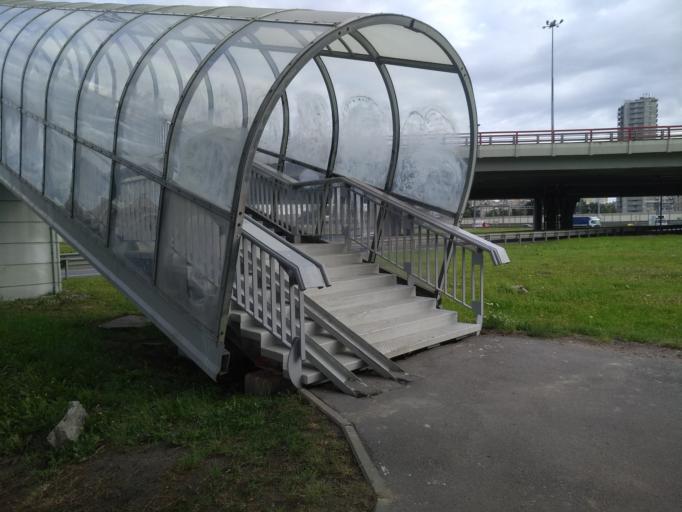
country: RU
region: St.-Petersburg
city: Shushary
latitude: 59.8163
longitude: 30.3754
